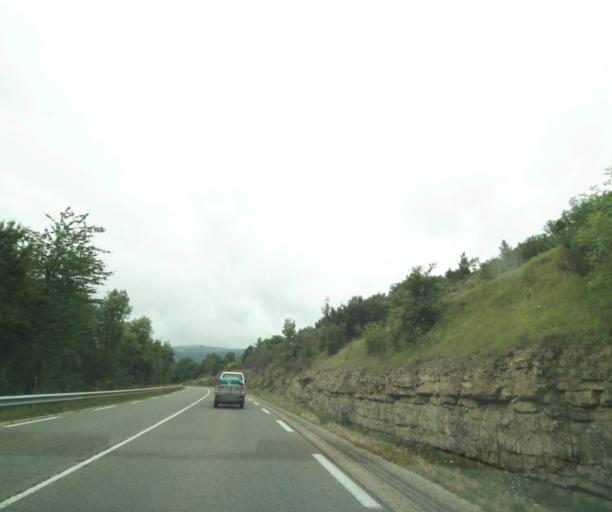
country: FR
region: Midi-Pyrenees
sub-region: Departement de l'Aveyron
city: Laissac
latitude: 44.3599
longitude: 2.9035
